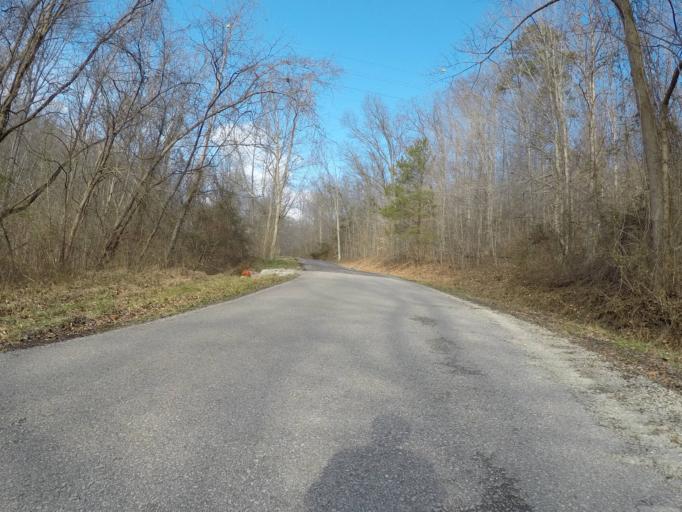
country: US
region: West Virginia
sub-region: Cabell County
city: Pea Ridge
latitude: 38.4273
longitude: -82.3390
